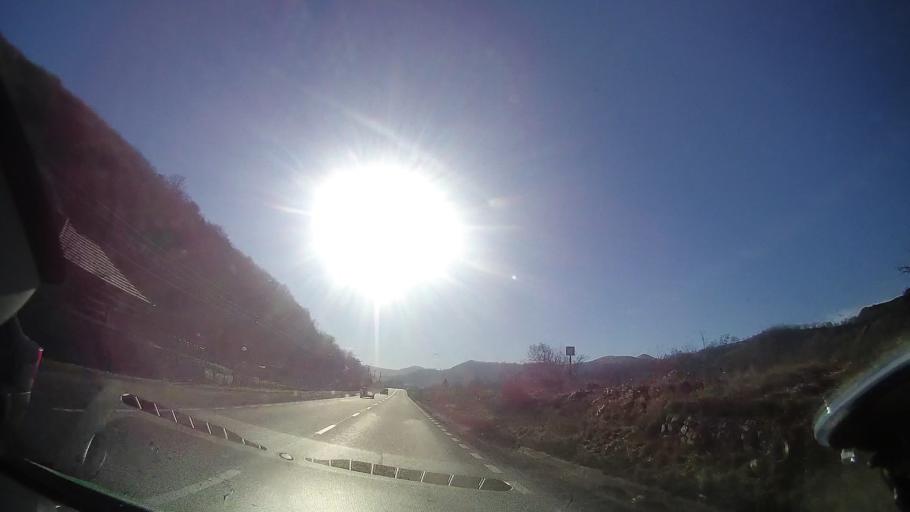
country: RO
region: Cluj
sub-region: Comuna Poeni
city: Poeni
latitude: 46.9072
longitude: 22.8663
